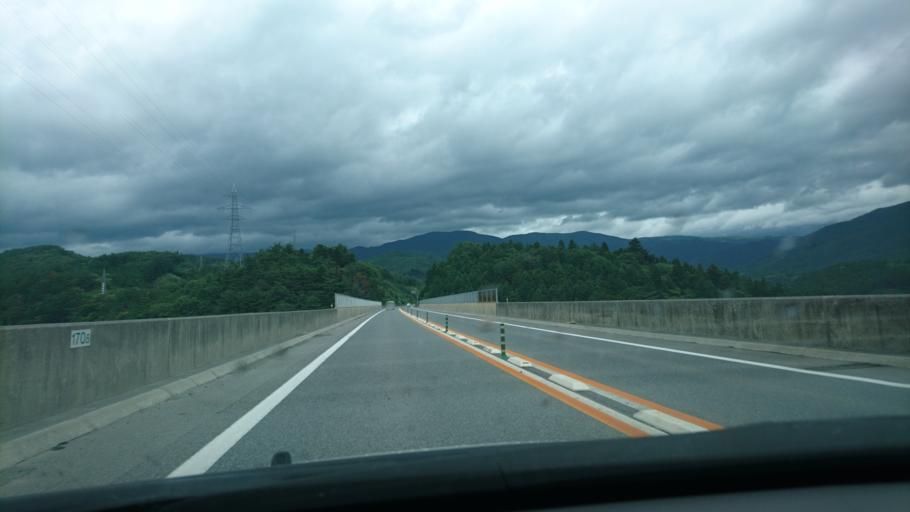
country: JP
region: Iwate
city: Ofunato
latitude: 39.0934
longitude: 141.7012
